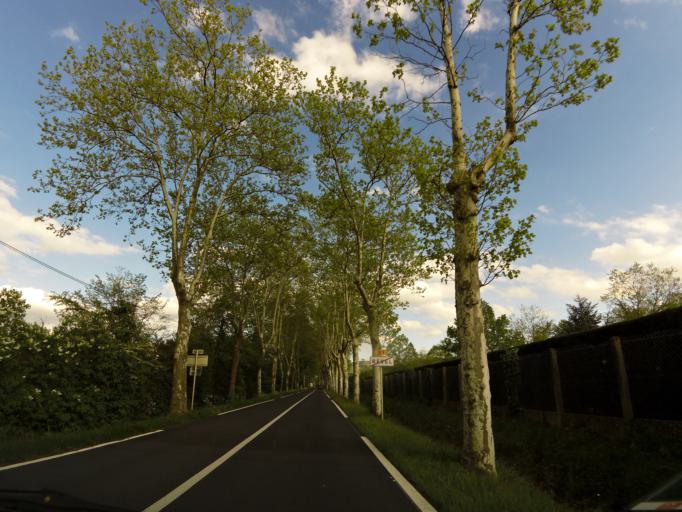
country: FR
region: Midi-Pyrenees
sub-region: Departement de la Haute-Garonne
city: Revel
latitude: 43.4547
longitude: 2.0163
